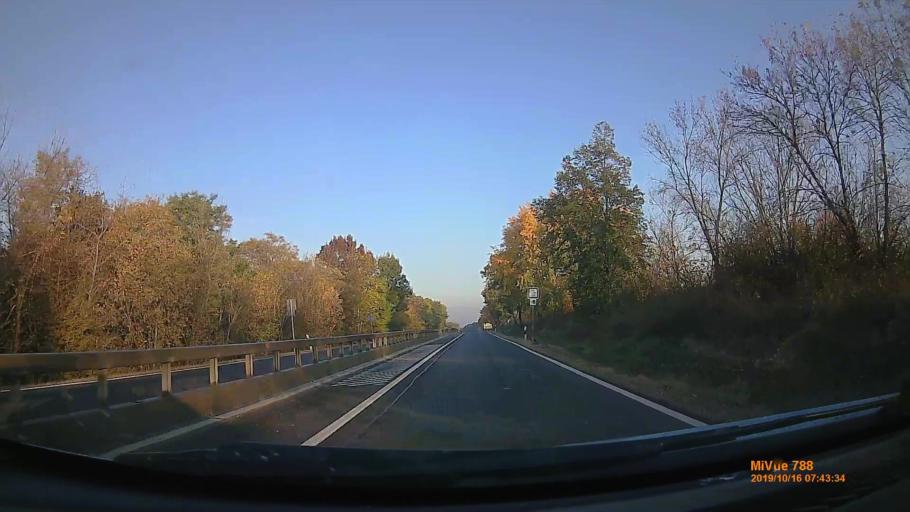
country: HU
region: Heves
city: Egerszalok
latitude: 47.8473
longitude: 20.3710
